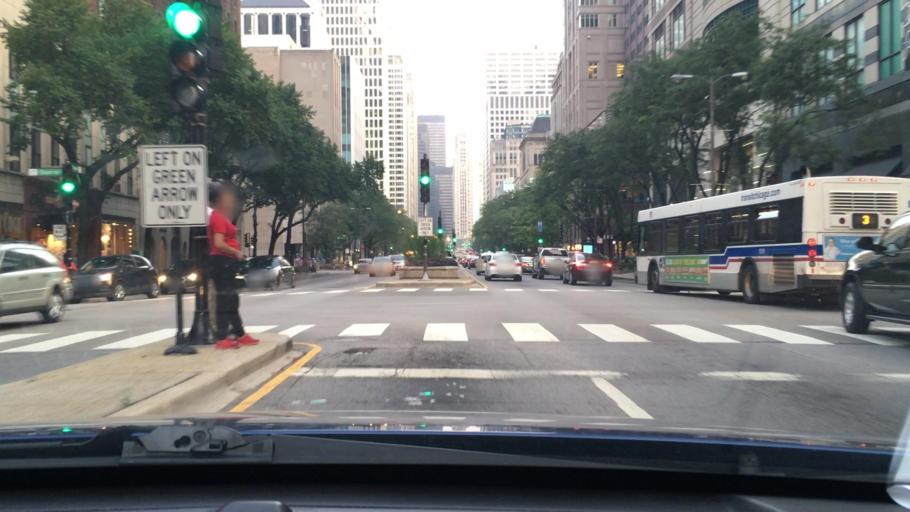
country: US
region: Illinois
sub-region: Cook County
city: Chicago
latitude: 41.8959
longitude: -87.6243
